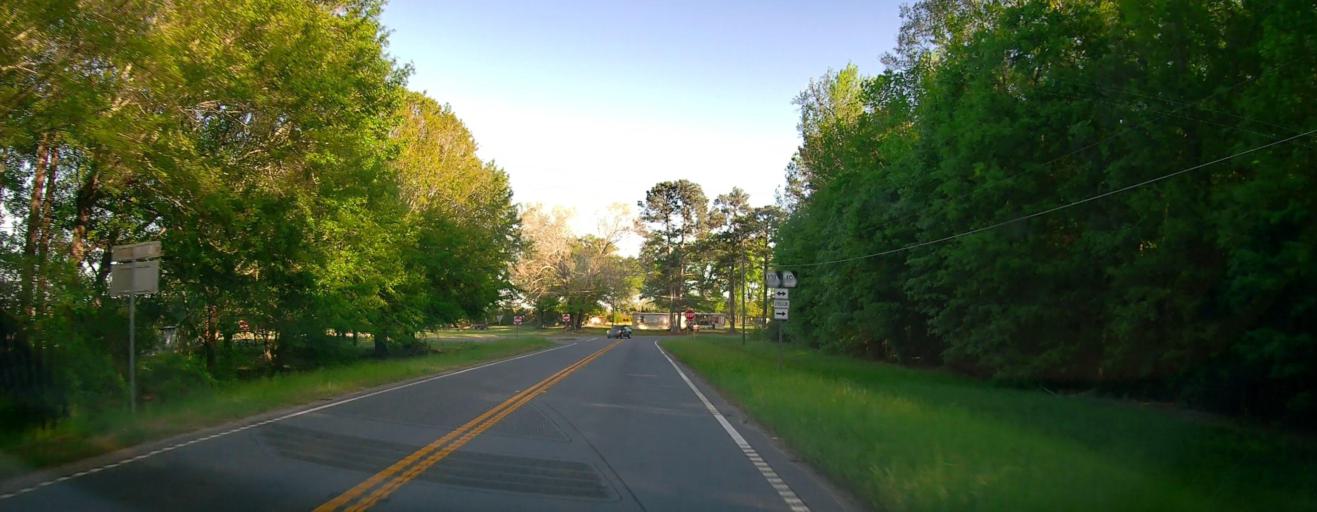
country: US
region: Georgia
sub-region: Macon County
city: Oglethorpe
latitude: 32.2841
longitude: -84.0725
